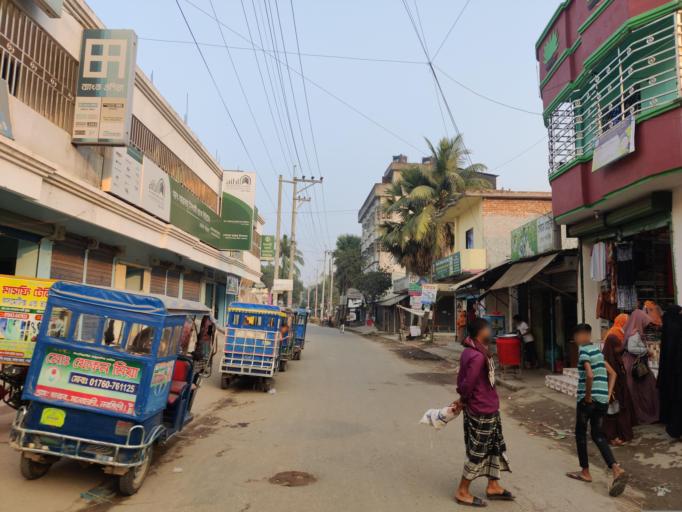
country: BD
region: Dhaka
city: Bajitpur
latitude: 24.1585
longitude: 90.7515
